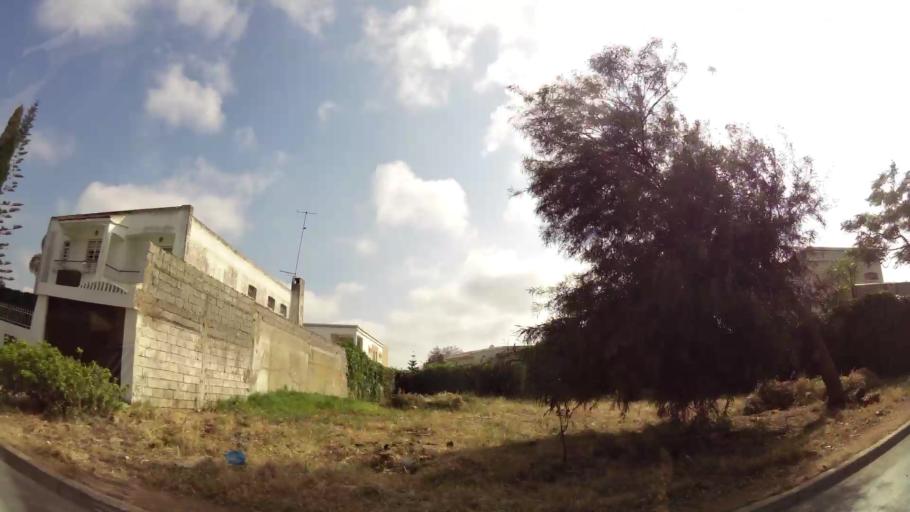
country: MA
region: Rabat-Sale-Zemmour-Zaer
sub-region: Rabat
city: Rabat
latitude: 33.9681
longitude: -6.8634
